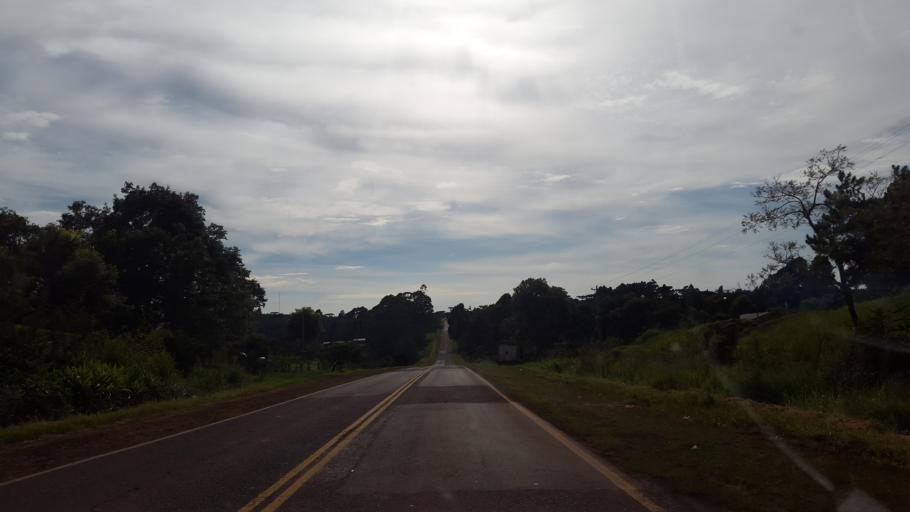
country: AR
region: Misiones
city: Bernardo de Irigoyen
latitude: -26.2765
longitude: -53.7161
